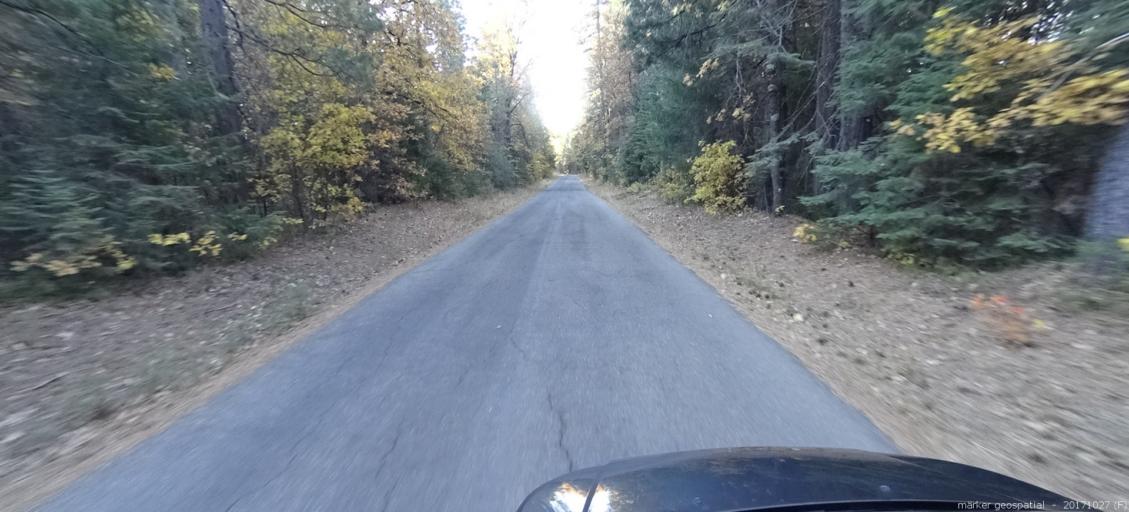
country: US
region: California
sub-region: Shasta County
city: Burney
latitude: 40.9284
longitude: -121.9492
